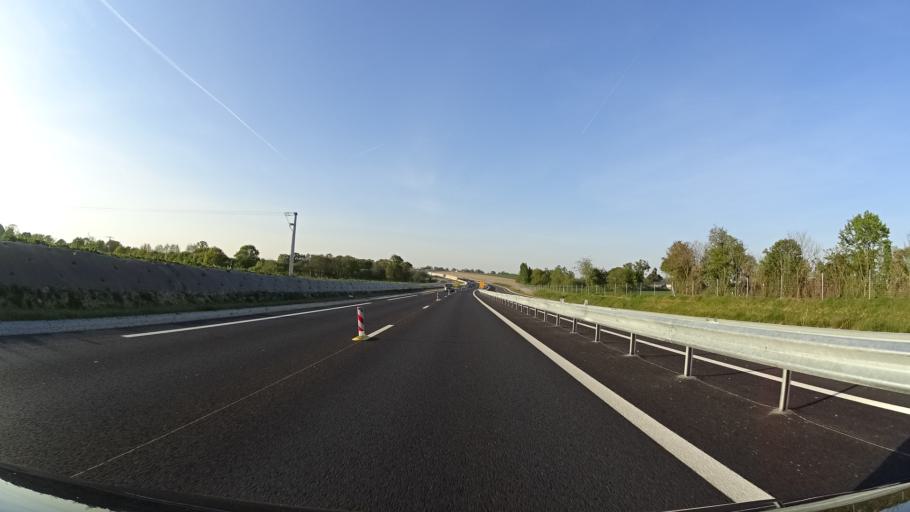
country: FR
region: Brittany
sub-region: Departement d'Ille-et-Vilaine
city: Pipriac
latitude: 47.7939
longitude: -1.9238
